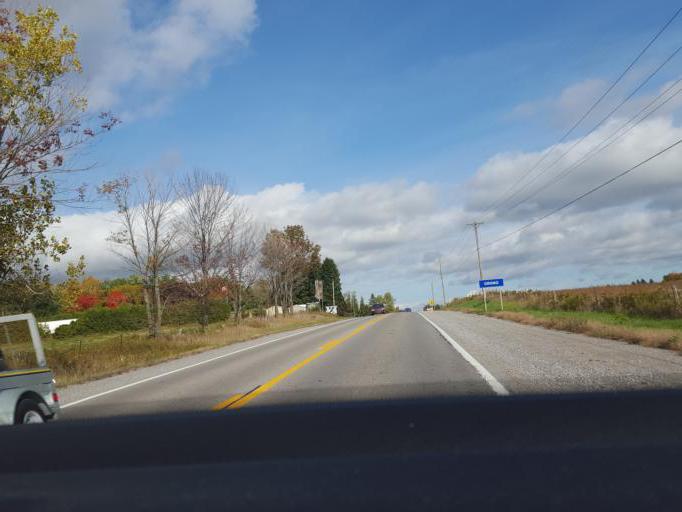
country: CA
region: Ontario
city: Oshawa
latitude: 43.9893
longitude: -78.6281
